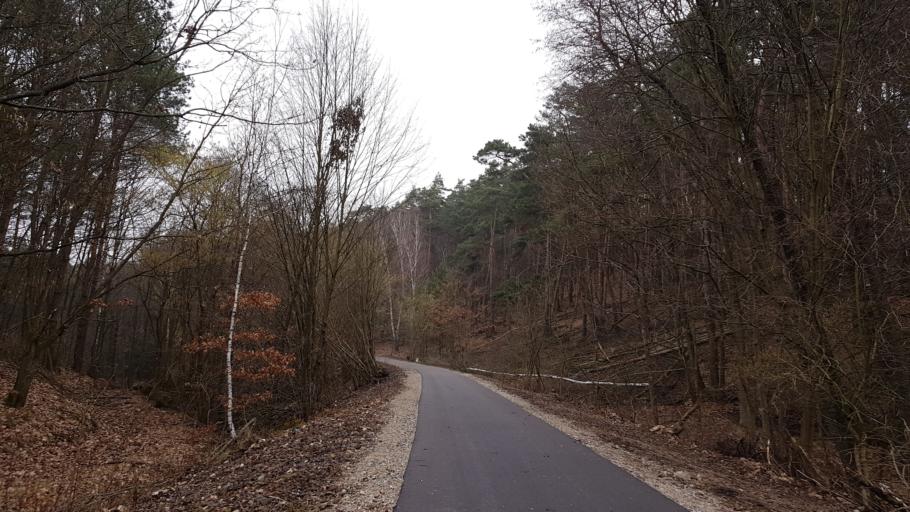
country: PL
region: West Pomeranian Voivodeship
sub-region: Powiat mysliborski
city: Barlinek
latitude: 53.0065
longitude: 15.2433
